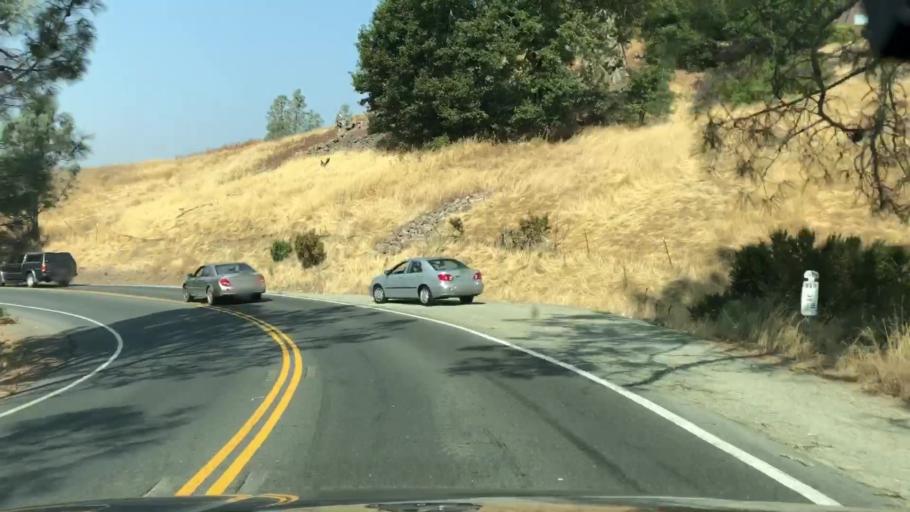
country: US
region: California
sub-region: Napa County
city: Calistoga
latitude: 38.6082
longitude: -122.5949
